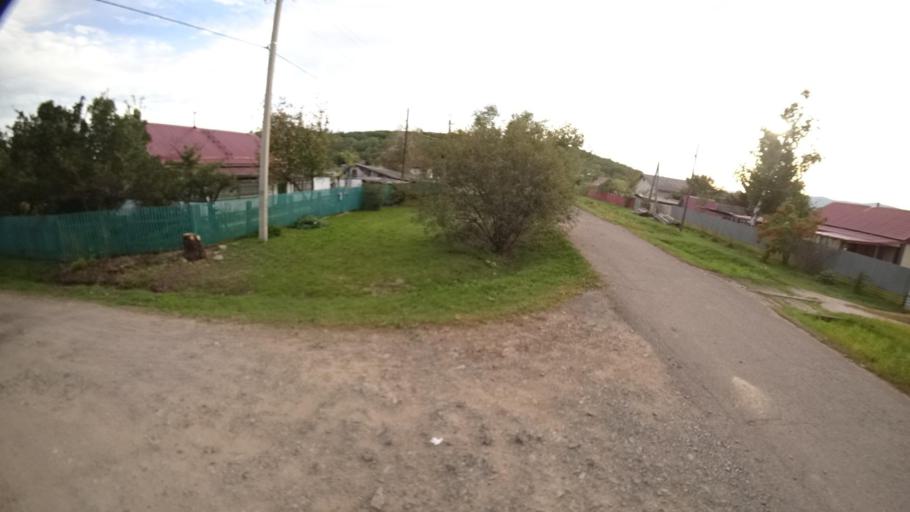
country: RU
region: Primorskiy
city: Yakovlevka
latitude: 44.4203
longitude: 133.4679
